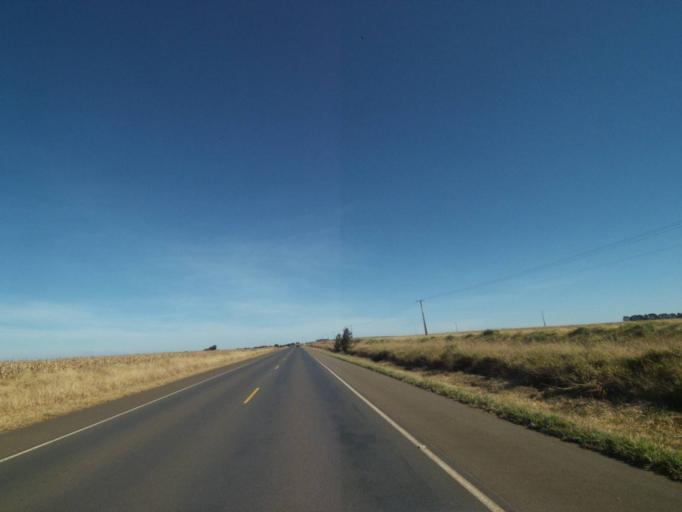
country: BR
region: Parana
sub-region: Tibagi
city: Tibagi
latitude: -24.3525
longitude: -50.3146
